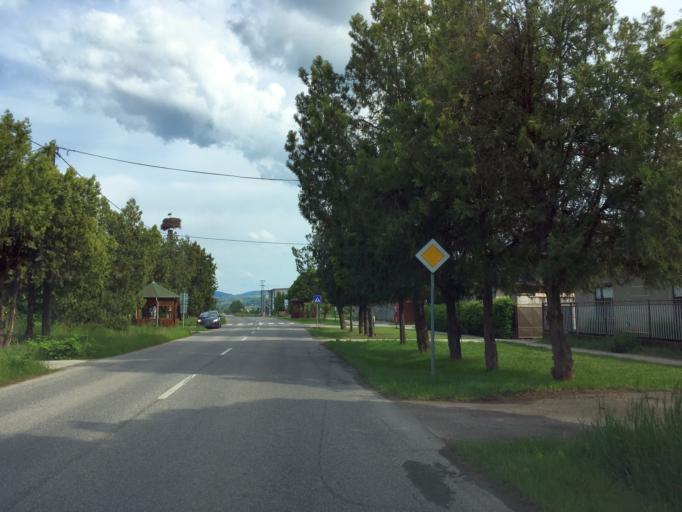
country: HU
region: Komarom-Esztergom
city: Dunaalmas
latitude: 47.7524
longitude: 18.3240
